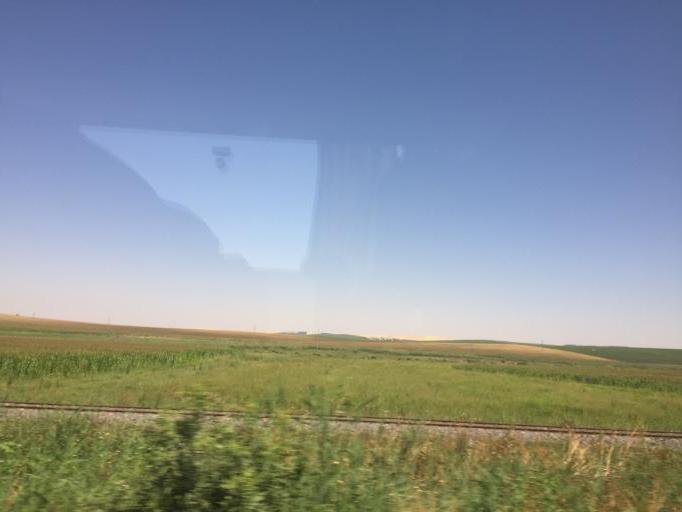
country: TR
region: Diyarbakir
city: Tepe
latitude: 37.8503
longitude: 40.7391
